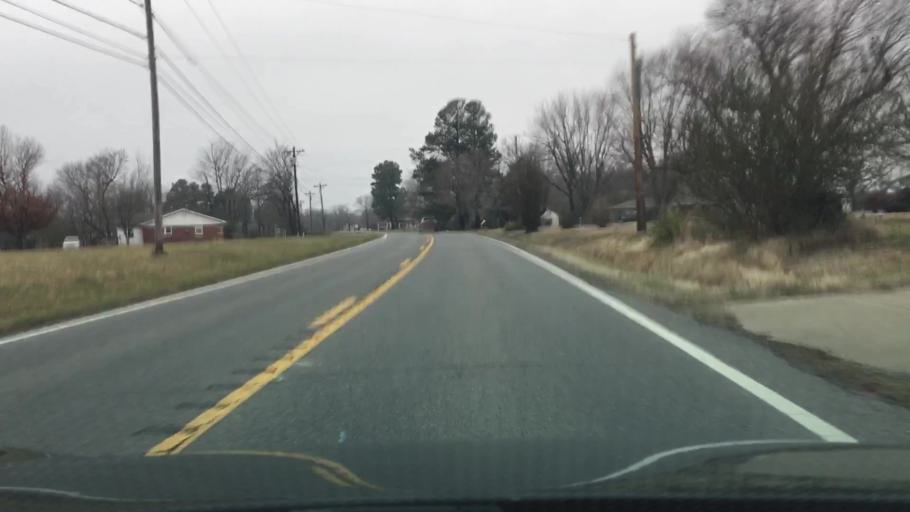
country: US
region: Kentucky
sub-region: Marshall County
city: Calvert City
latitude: 36.9713
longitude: -88.3917
